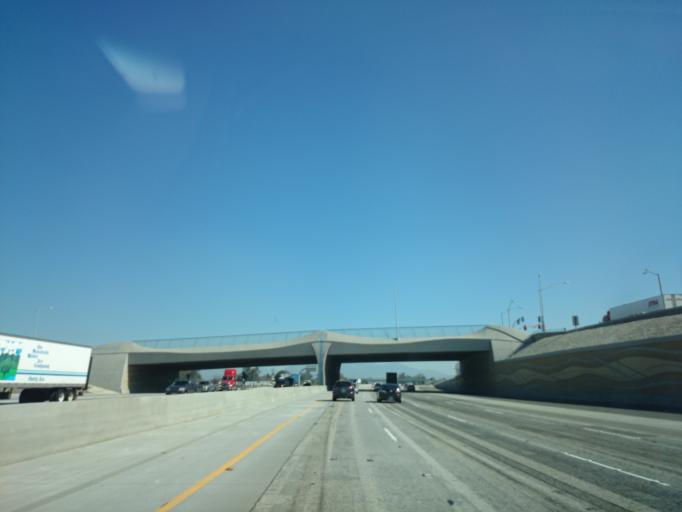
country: US
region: California
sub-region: San Bernardino County
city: Fontana
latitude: 34.0668
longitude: -117.4551
